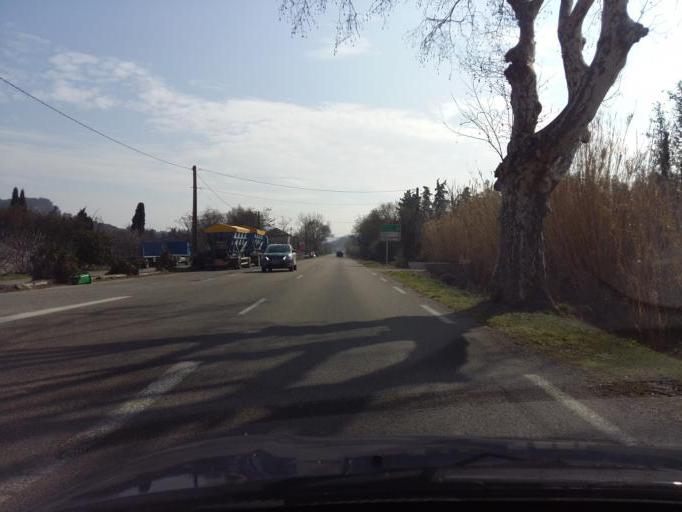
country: FR
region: Provence-Alpes-Cote d'Azur
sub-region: Departement des Bouches-du-Rhone
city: Orgon
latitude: 43.8055
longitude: 4.9989
